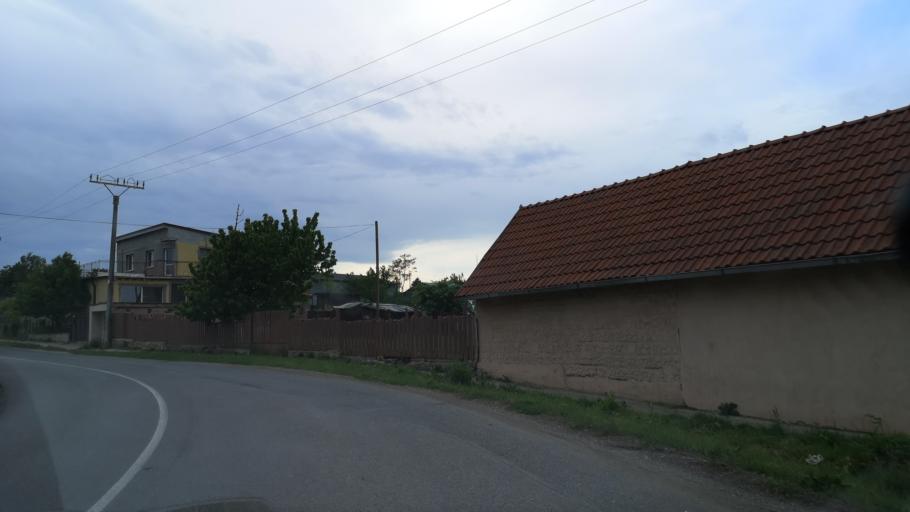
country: SK
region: Nitriansky
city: Sellye
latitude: 48.2407
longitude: 17.9161
